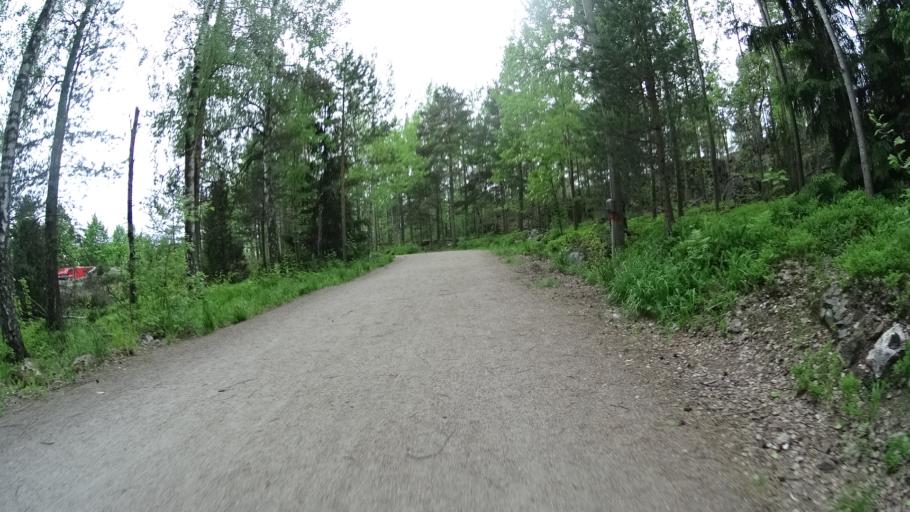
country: FI
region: Uusimaa
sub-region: Helsinki
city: Vantaa
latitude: 60.2466
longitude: 25.0744
